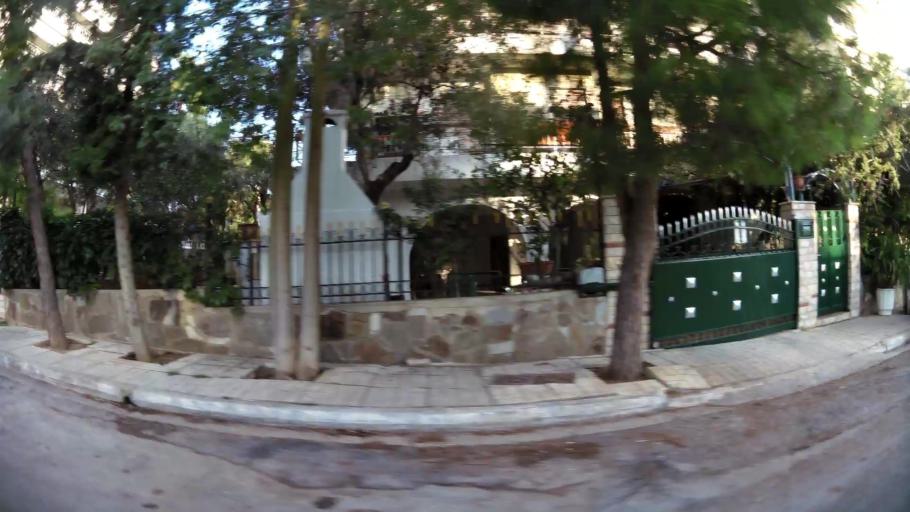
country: GR
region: Attica
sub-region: Nomarchia Athinas
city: Argyroupoli
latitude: 37.9003
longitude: 23.7740
